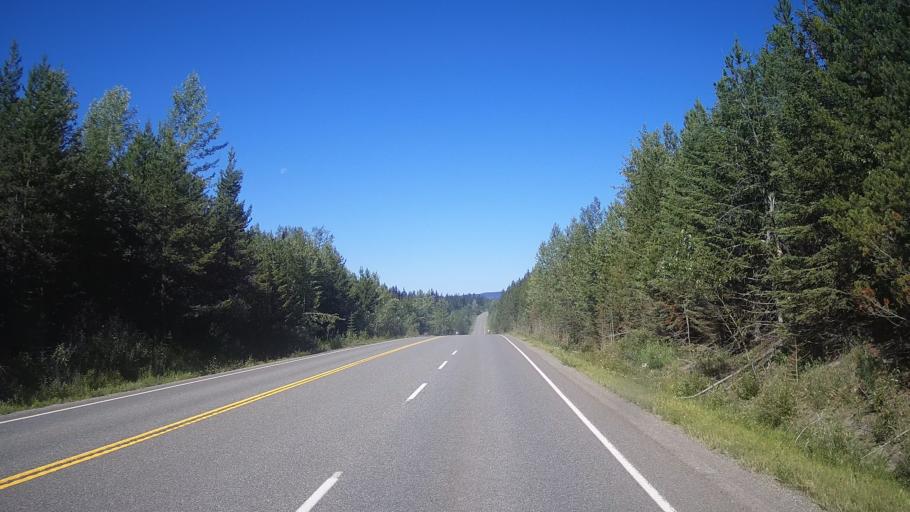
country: CA
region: British Columbia
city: Kamloops
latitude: 51.4973
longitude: -120.3772
